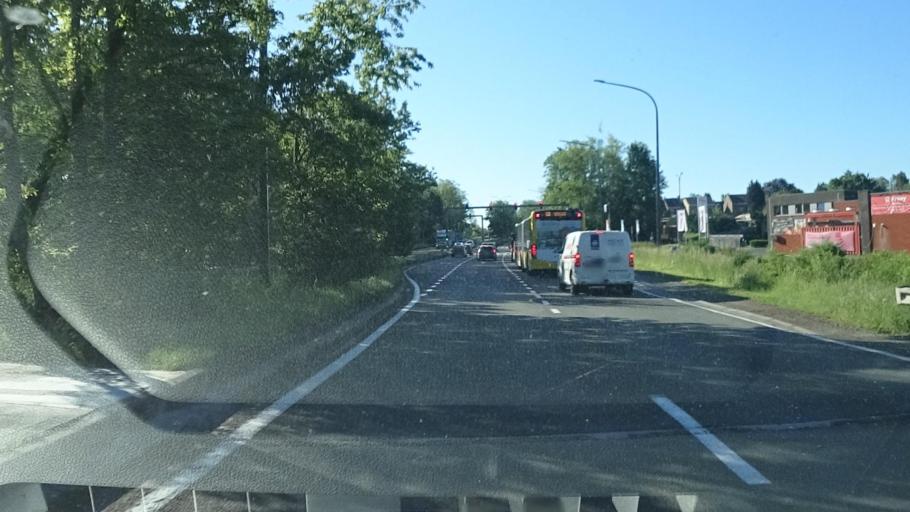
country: BE
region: Wallonia
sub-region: Province du Hainaut
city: Binche
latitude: 50.4536
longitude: 4.1537
